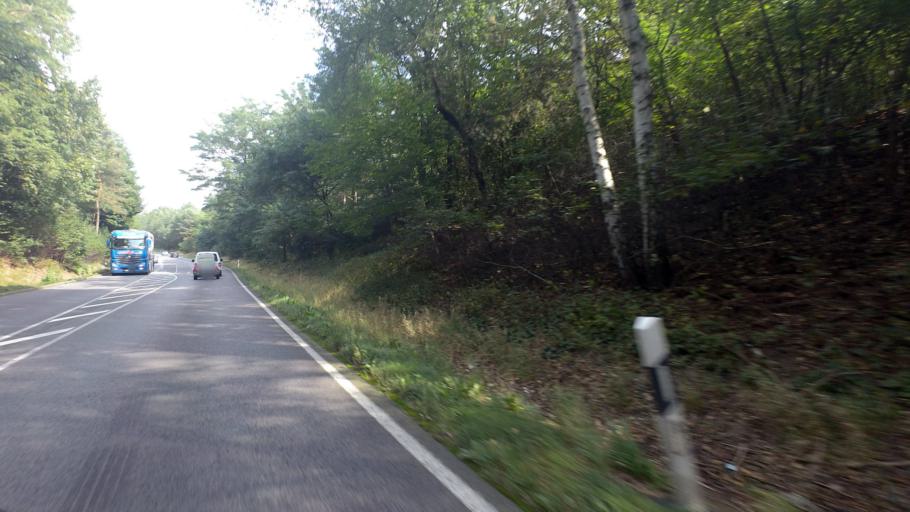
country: DE
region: Brandenburg
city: Elsterwerda
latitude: 51.4743
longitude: 13.4974
